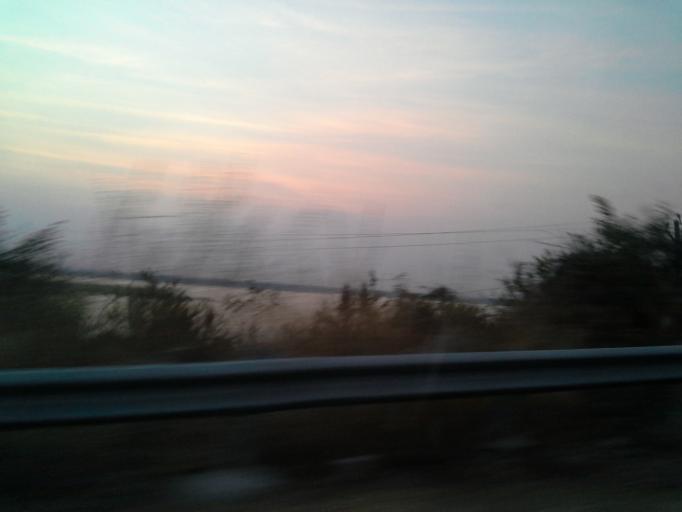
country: IN
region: Telangana
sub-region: Hyderabad
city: Hyderabad
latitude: 17.3193
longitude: 78.3710
